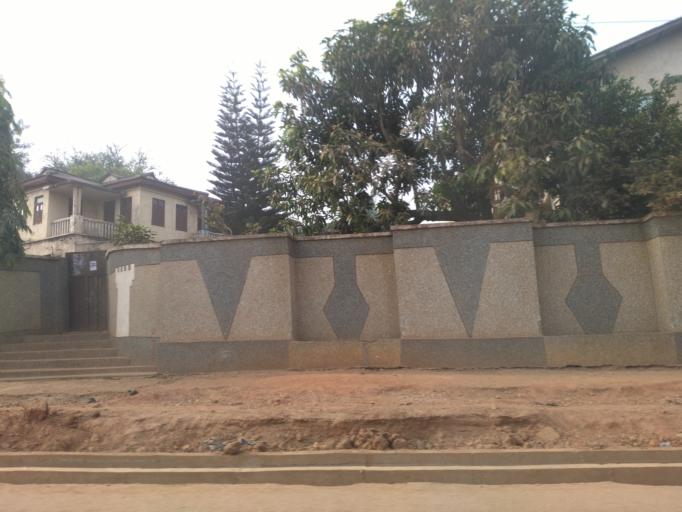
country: GH
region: Ashanti
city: Kumasi
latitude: 6.7086
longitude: -1.6254
